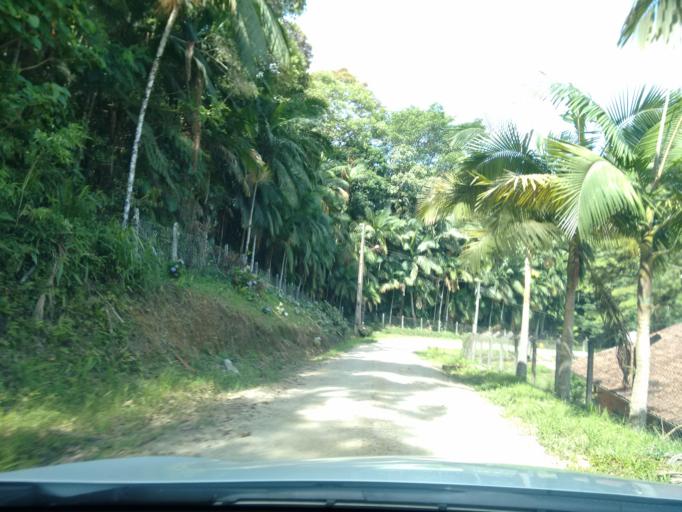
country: BR
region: Santa Catarina
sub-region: Pomerode
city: Pomerode
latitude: -26.7138
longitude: -49.0911
